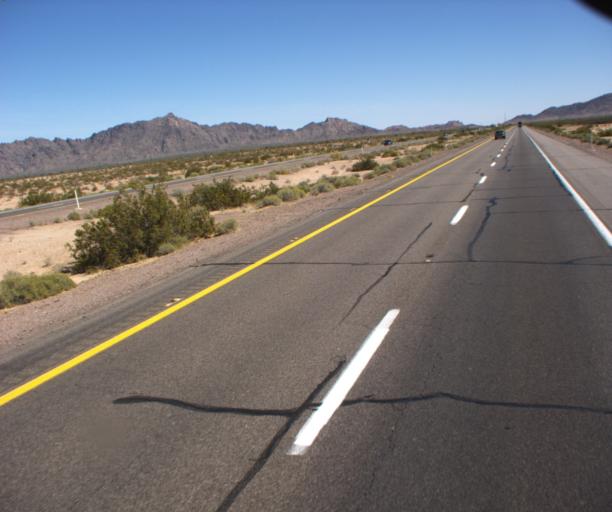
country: US
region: Arizona
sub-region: Yuma County
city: Wellton
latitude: 32.7151
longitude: -113.8103
